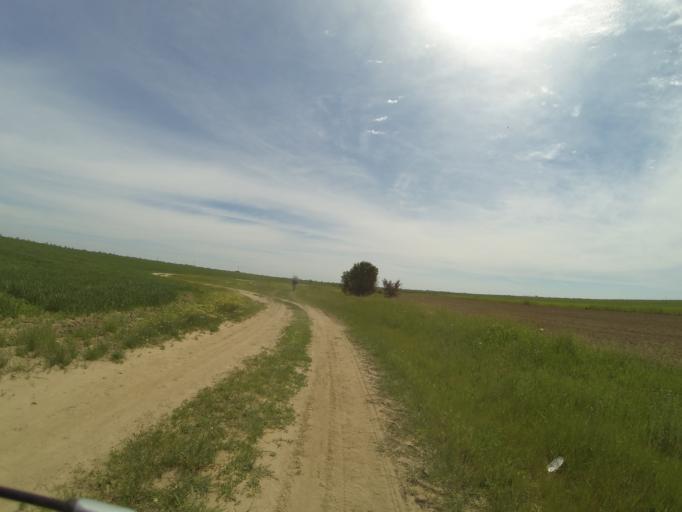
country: RO
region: Dolj
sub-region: Comuna Ghindeni
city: Ghindeni
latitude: 44.2066
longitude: 23.9538
